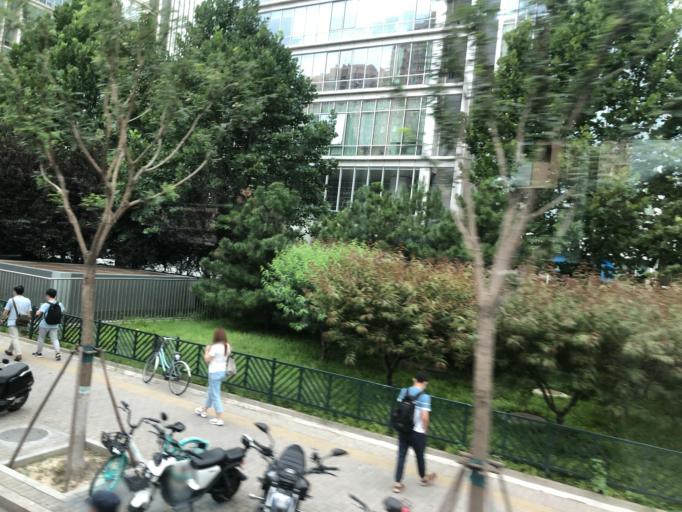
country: CN
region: Beijing
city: Jinrongjie
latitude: 39.9333
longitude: 116.3191
